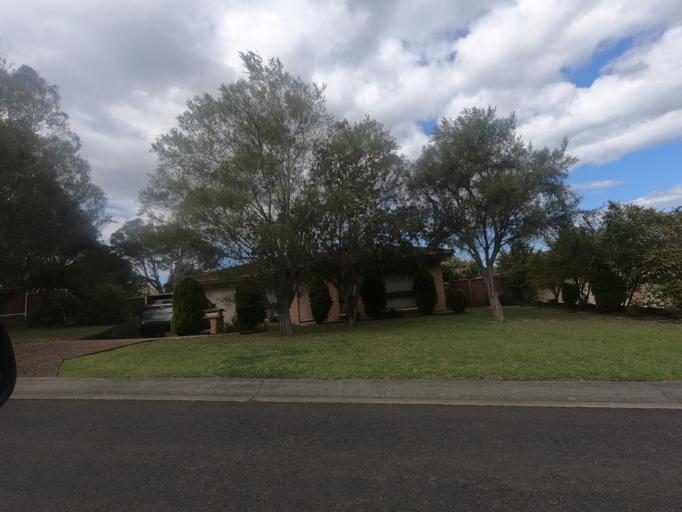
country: AU
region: New South Wales
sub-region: Wollongong
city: Dapto
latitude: -34.4890
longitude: 150.7765
